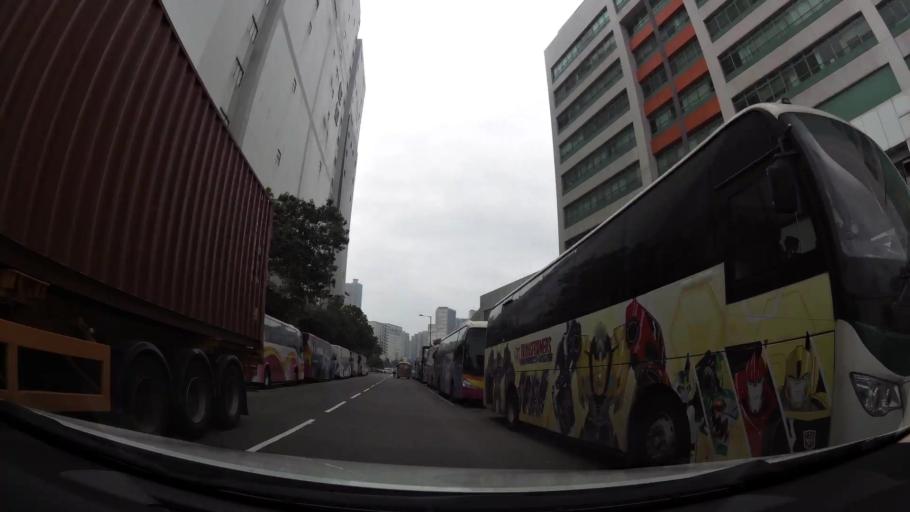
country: HK
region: Wanchai
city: Wan Chai
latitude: 22.2731
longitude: 114.2430
